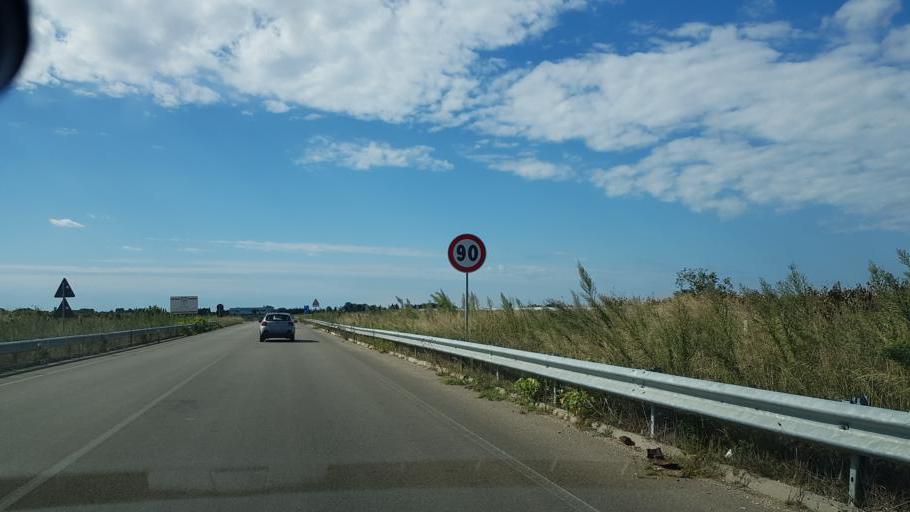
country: IT
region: Apulia
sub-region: Provincia di Lecce
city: Leverano
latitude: 40.2974
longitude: 17.9742
